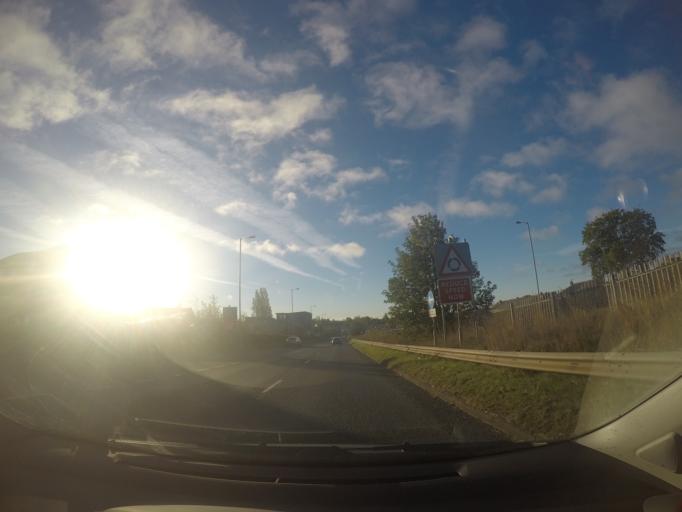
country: GB
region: England
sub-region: City and Borough of Leeds
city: Scholes
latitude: 53.8184
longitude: -1.4542
